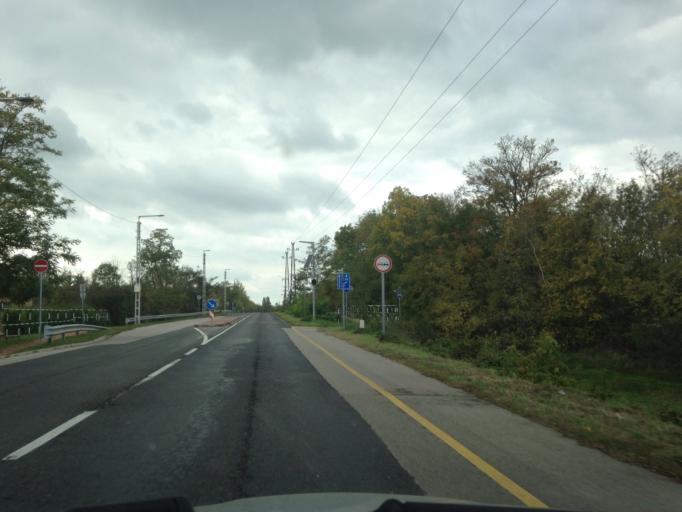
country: AT
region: Burgenland
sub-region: Politischer Bezirk Neusiedl am See
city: Nickelsdorf
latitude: 47.9187
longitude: 17.1412
